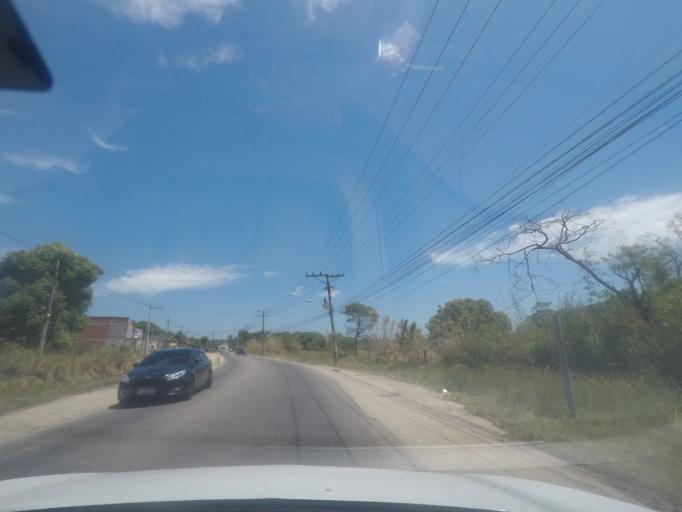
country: BR
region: Rio de Janeiro
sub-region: Itaguai
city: Itaguai
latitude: -22.9885
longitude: -43.6520
